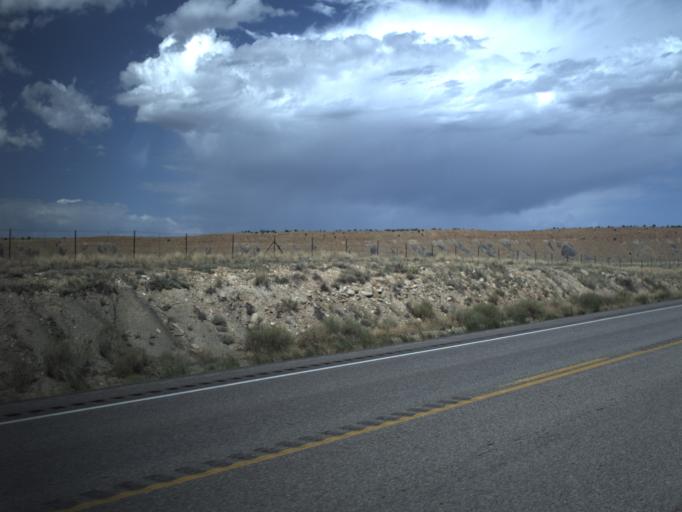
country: US
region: Utah
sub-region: Carbon County
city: East Carbon City
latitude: 39.3859
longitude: -110.4105
